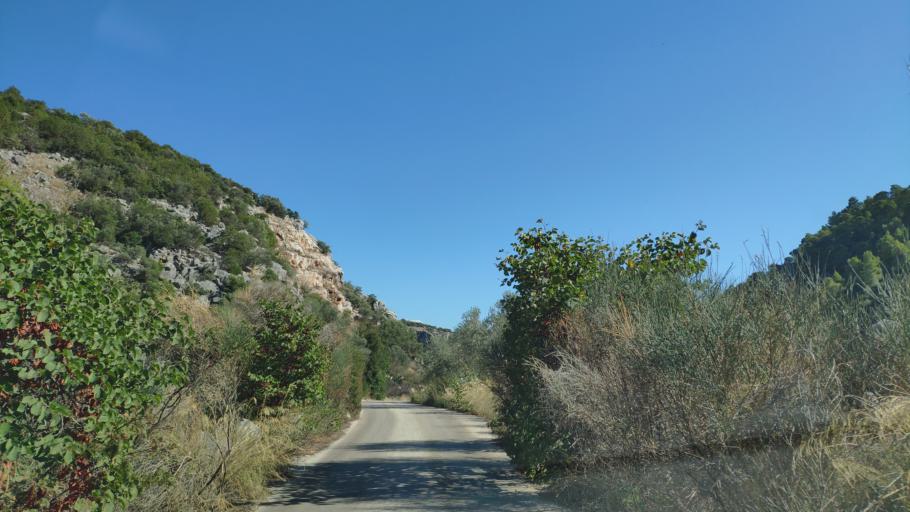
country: GR
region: Peloponnese
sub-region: Nomos Korinthias
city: Sofikon
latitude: 37.7337
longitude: 23.1115
